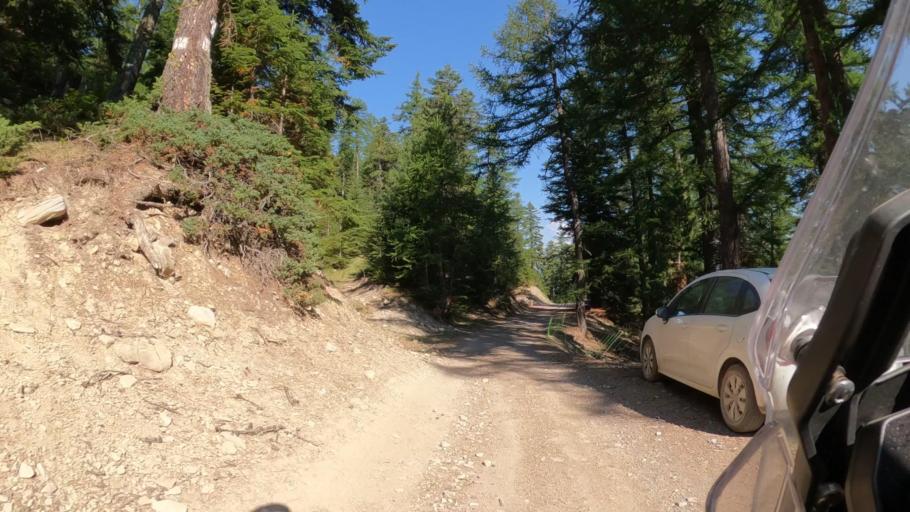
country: FR
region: Provence-Alpes-Cote d'Azur
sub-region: Departement des Hautes-Alpes
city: Embrun
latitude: 44.5904
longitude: 6.5828
